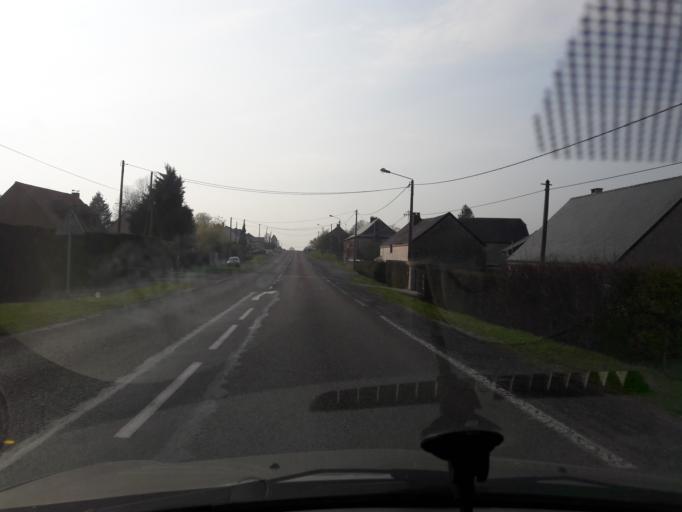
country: FR
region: Nord-Pas-de-Calais
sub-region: Departement du Nord
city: Marpent
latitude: 50.2523
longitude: 4.0899
